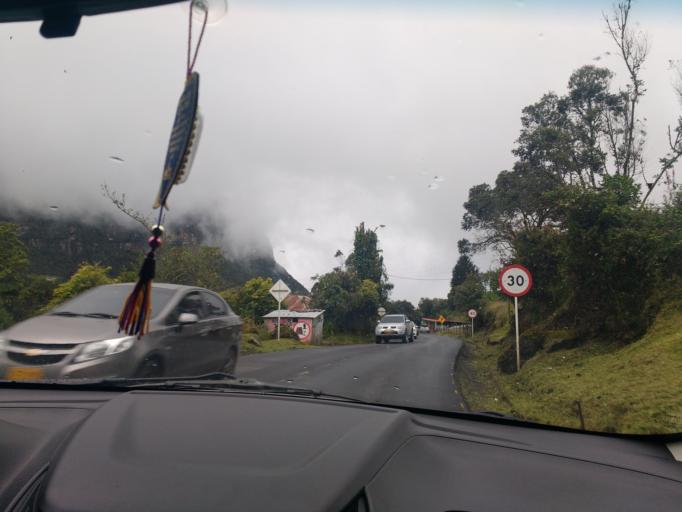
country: CO
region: Cundinamarca
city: Choachi
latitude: 4.5659
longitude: -73.9727
